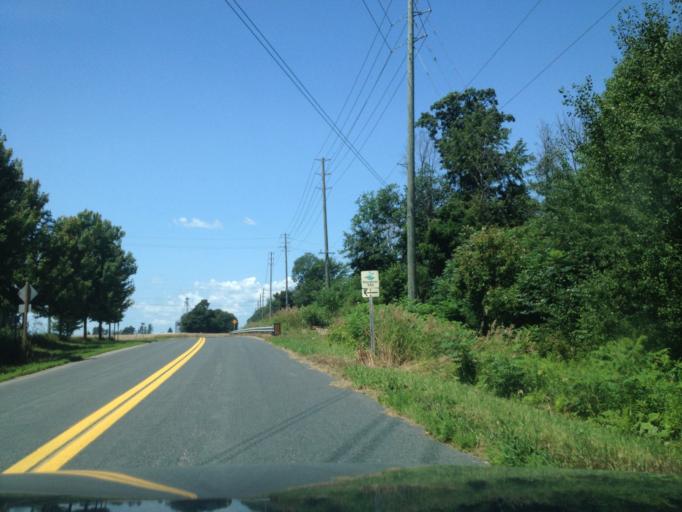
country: CA
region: Ontario
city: Aylmer
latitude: 42.6483
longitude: -80.7592
